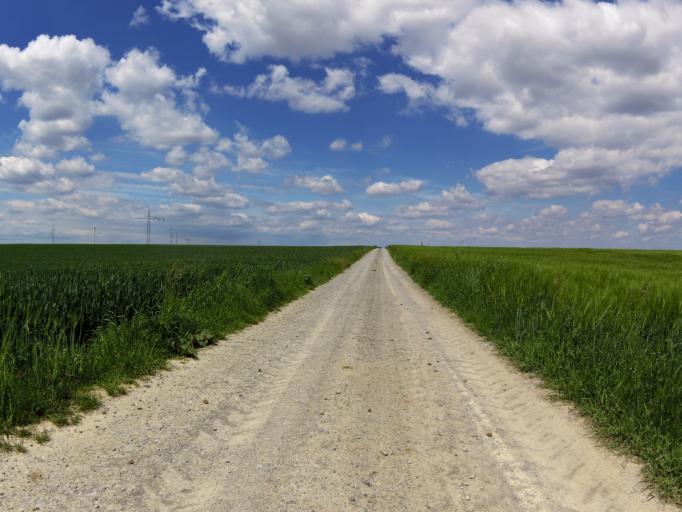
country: DE
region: Bavaria
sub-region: Regierungsbezirk Unterfranken
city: Theilheim
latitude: 49.7352
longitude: 10.0649
